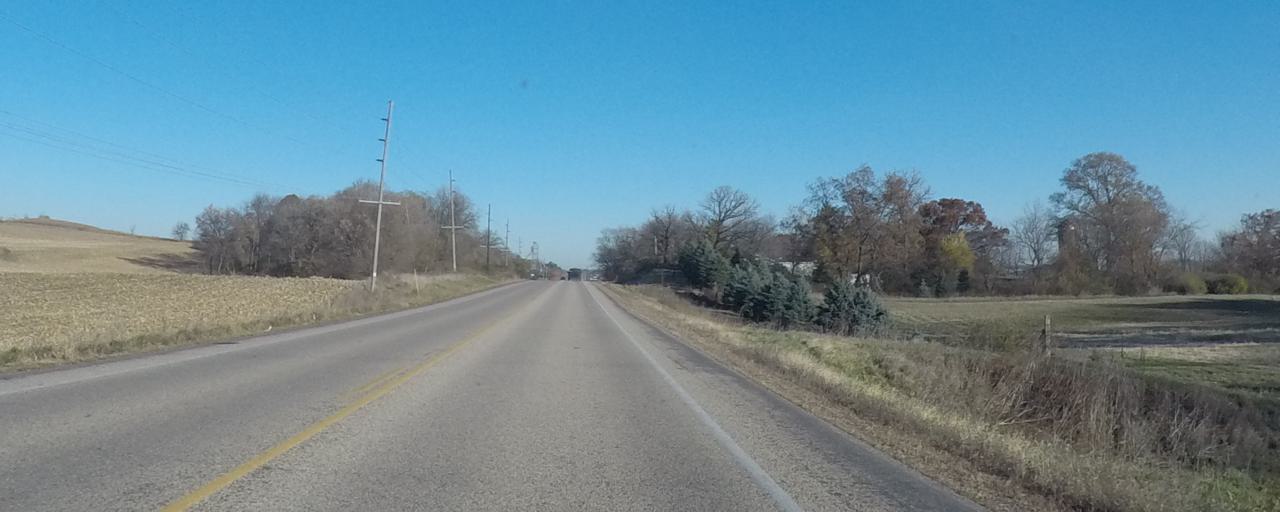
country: US
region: Wisconsin
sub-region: Dane County
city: Cottage Grove
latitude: 43.0540
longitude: -89.1998
